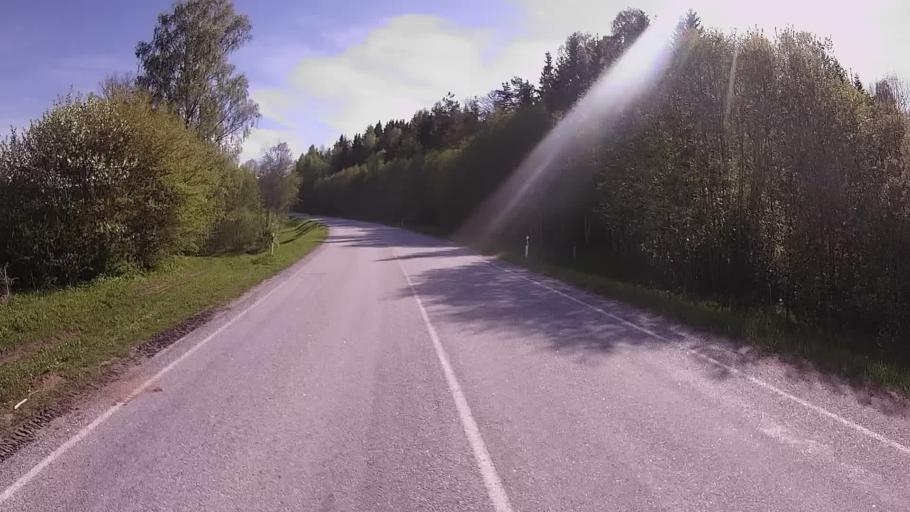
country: EE
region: Vorumaa
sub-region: Antsla vald
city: Vana-Antsla
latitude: 58.0196
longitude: 26.5008
